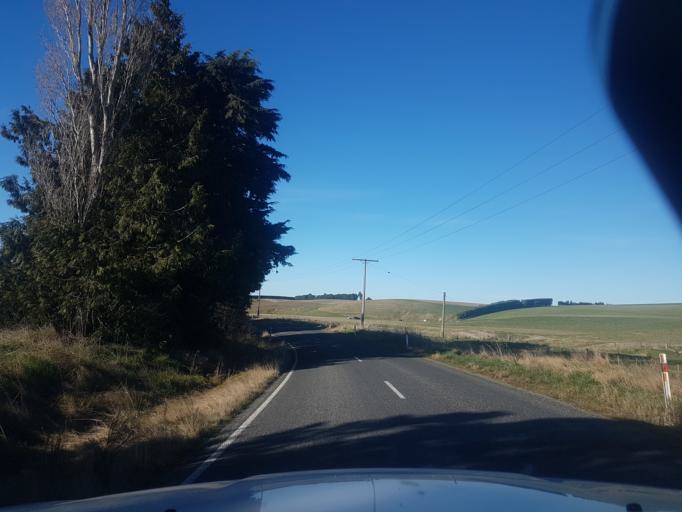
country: NZ
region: Canterbury
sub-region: Timaru District
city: Pleasant Point
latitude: -44.2760
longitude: 171.1178
